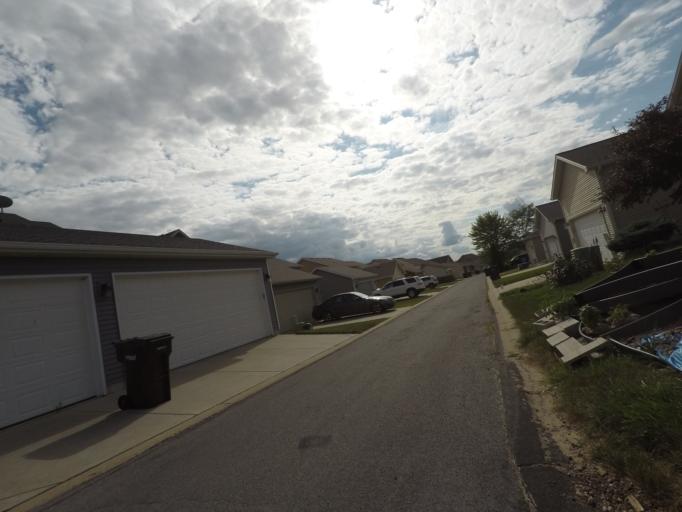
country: US
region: Wisconsin
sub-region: Dane County
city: Middleton
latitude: 43.0558
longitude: -89.5473
